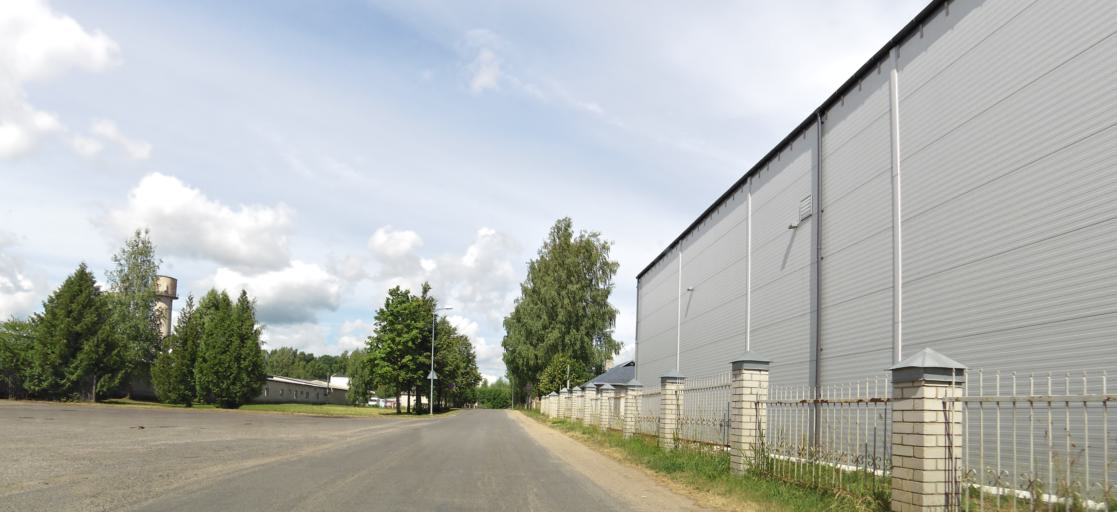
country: LT
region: Panevezys
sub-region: Birzai
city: Birzai
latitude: 56.1863
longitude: 24.7407
